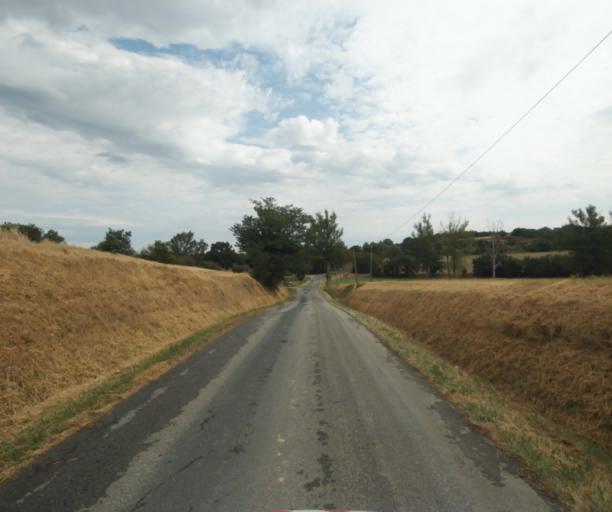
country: FR
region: Midi-Pyrenees
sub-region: Departement de la Haute-Garonne
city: Revel
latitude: 43.4389
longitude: 1.9709
